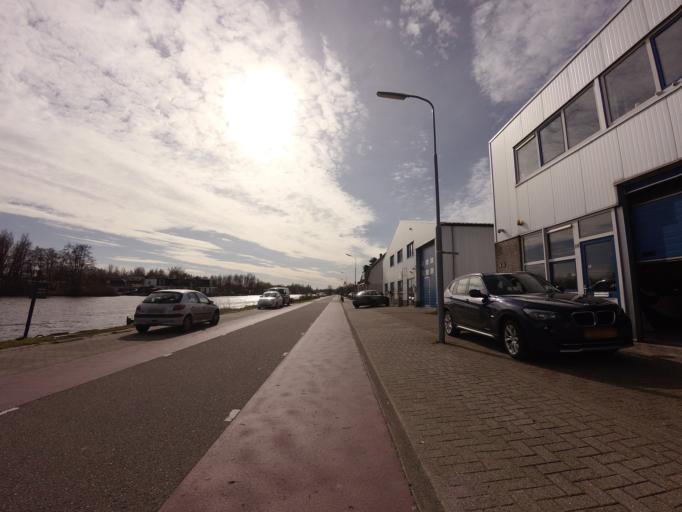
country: NL
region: North Holland
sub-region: Gemeente Aalsmeer
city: Aalsmeer
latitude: 52.2862
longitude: 4.7839
